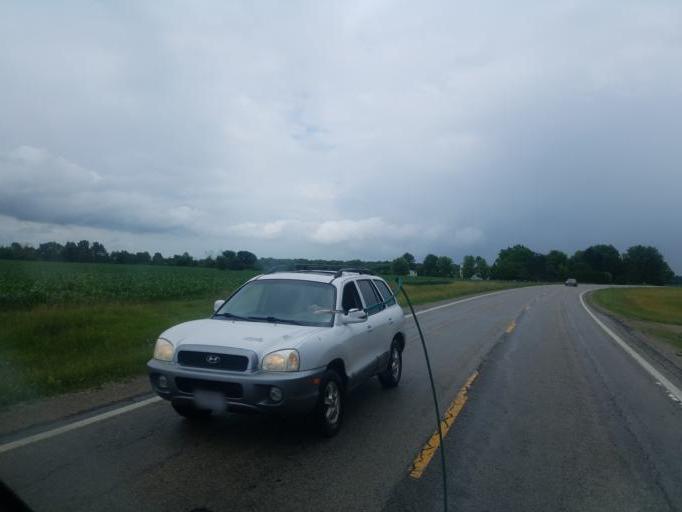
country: US
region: Ohio
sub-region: Morrow County
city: Cardington
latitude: 40.5162
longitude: -82.9279
